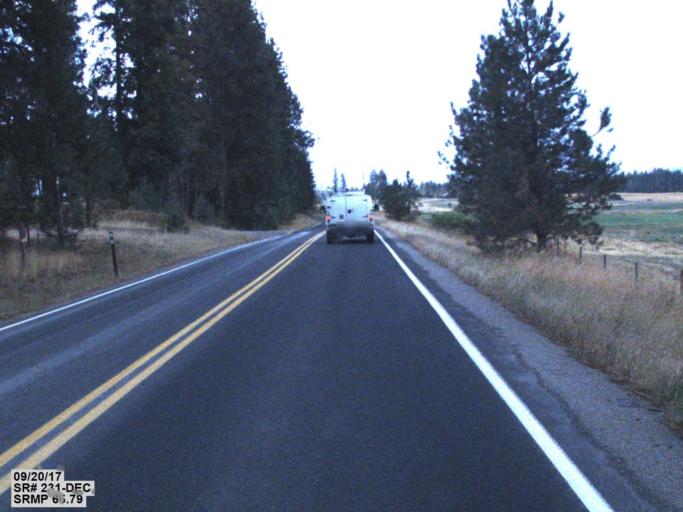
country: US
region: Washington
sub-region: Stevens County
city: Chewelah
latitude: 48.0968
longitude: -117.7579
